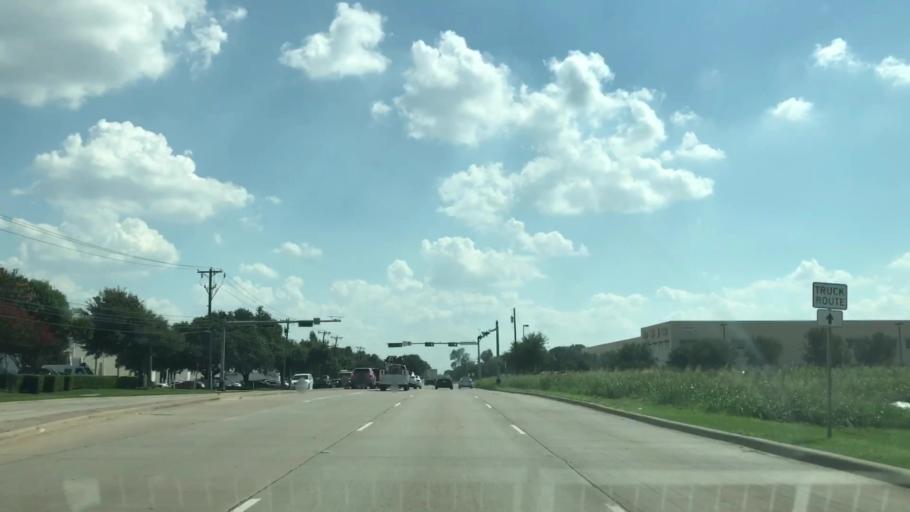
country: US
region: Texas
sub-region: Dallas County
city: Farmers Branch
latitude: 32.9381
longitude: -96.9252
